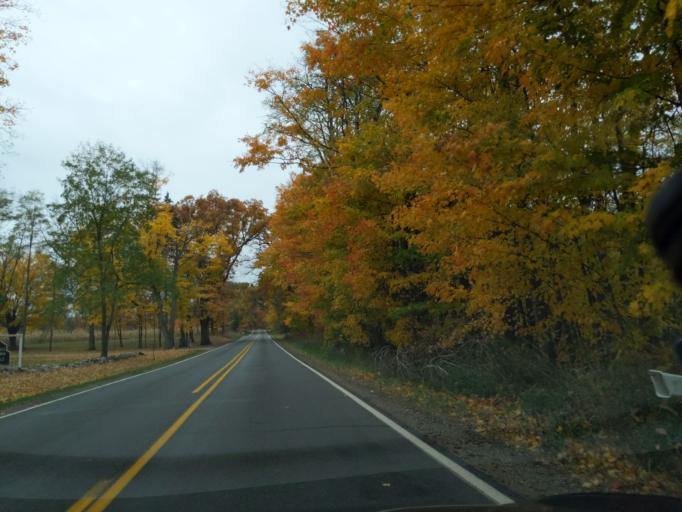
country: US
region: Michigan
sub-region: Jackson County
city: Spring Arbor
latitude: 42.3053
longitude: -84.6002
